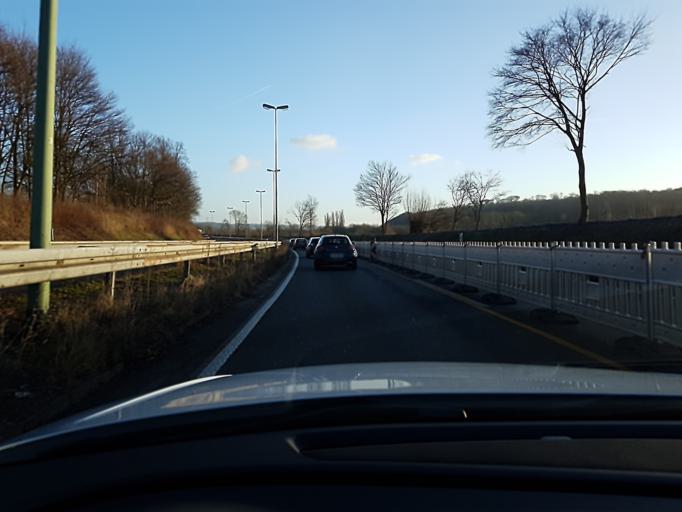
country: DE
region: North Rhine-Westphalia
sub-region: Regierungsbezirk Dusseldorf
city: Essen
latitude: 51.4252
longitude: 7.0610
